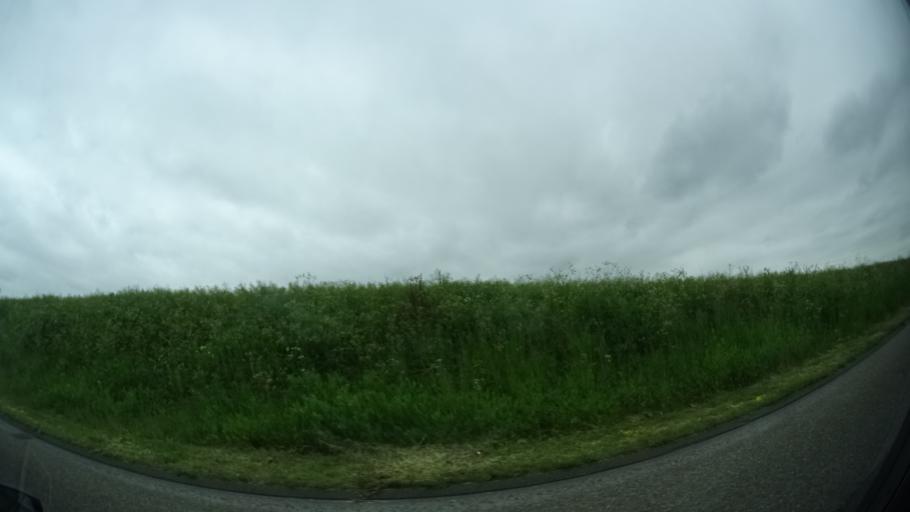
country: DK
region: Central Jutland
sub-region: Skanderborg Kommune
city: Horning
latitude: 56.1154
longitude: 10.0381
